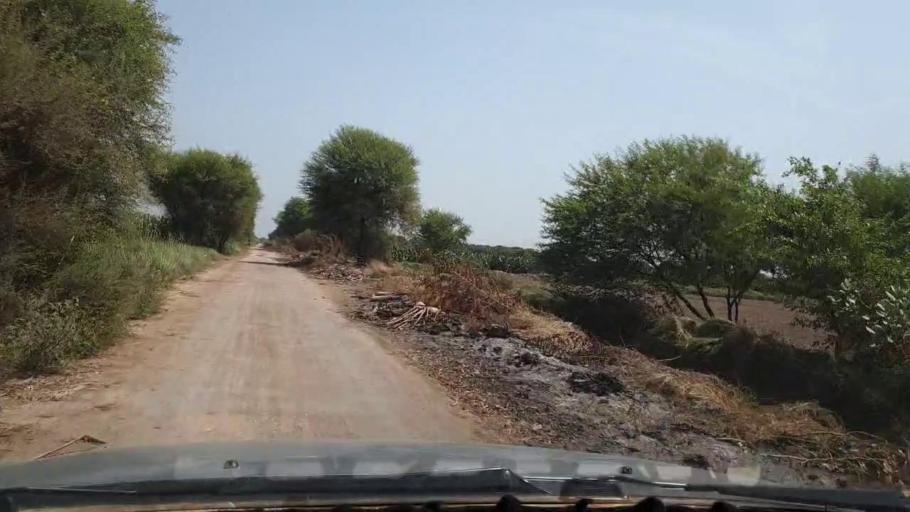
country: PK
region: Sindh
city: Tando Muhammad Khan
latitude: 25.1754
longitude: 68.6428
